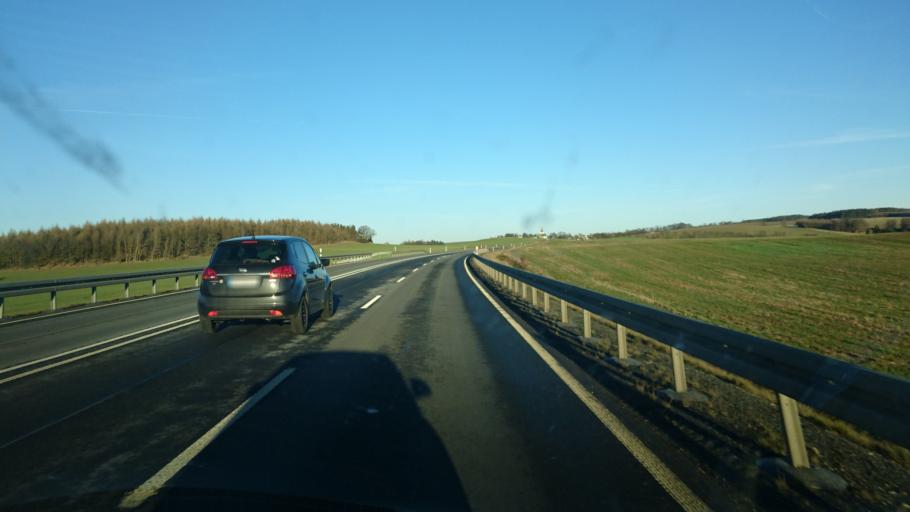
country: DE
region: Thuringia
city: Langenwolschendorf
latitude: 50.6242
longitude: 11.9317
